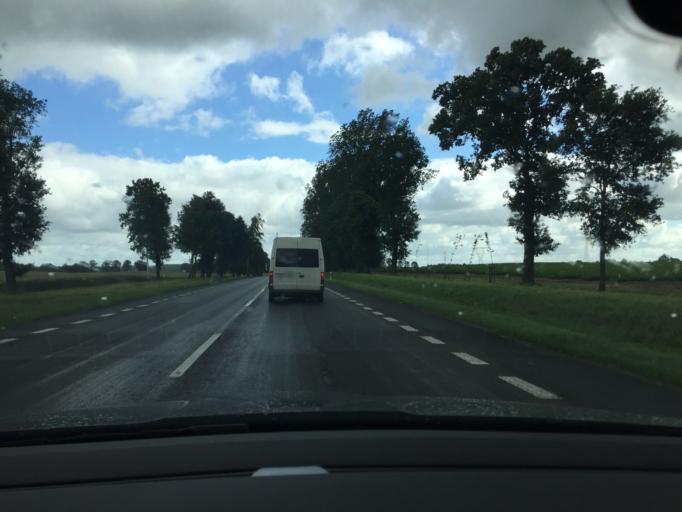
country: PL
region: West Pomeranian Voivodeship
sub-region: Koszalin
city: Koszalin
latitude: 54.1481
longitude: 16.0717
